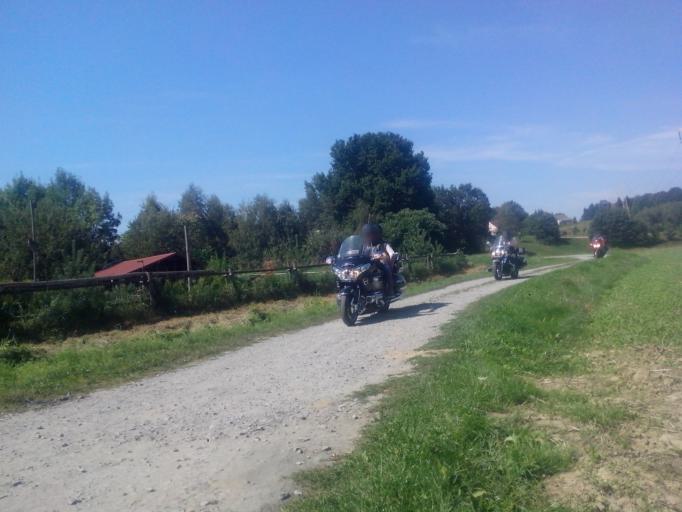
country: PL
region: Subcarpathian Voivodeship
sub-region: Powiat strzyzowski
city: Strzyzow
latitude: 49.8642
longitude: 21.7696
